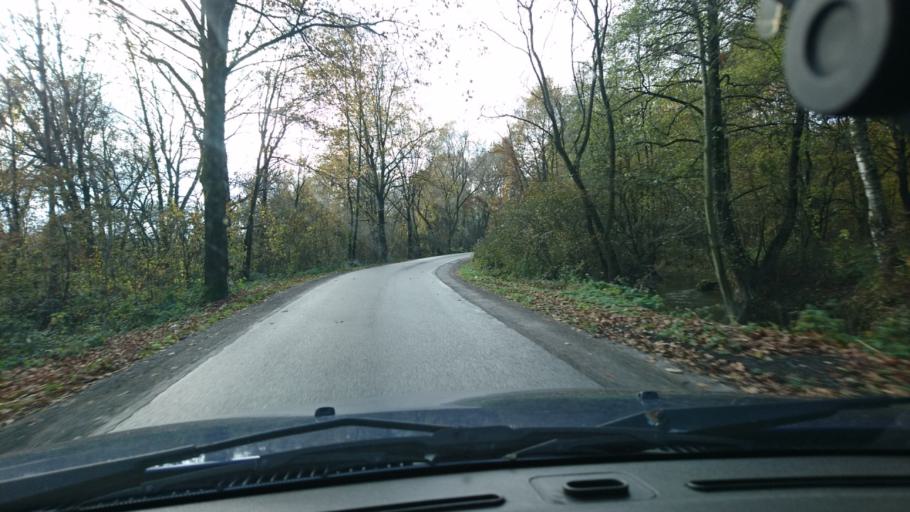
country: PL
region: Lesser Poland Voivodeship
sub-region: Powiat oswiecimski
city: Nowa Wies
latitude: 49.9342
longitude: 19.1889
